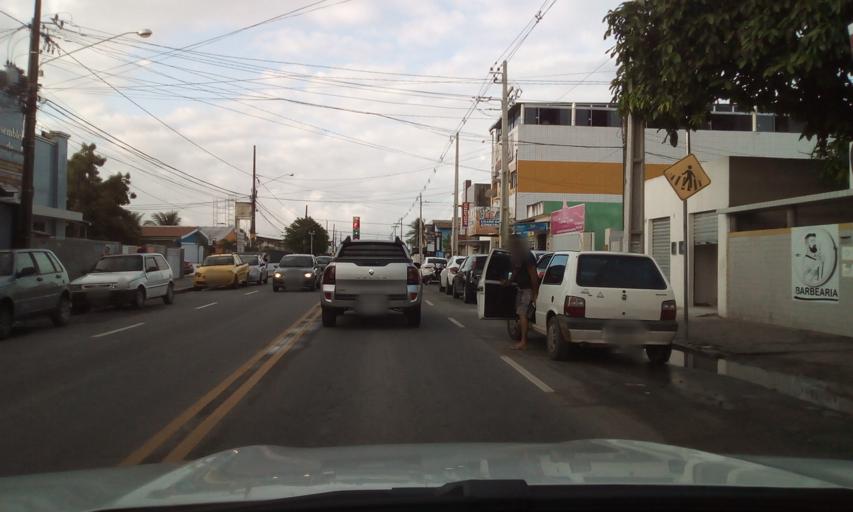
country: BR
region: Paraiba
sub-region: Joao Pessoa
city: Joao Pessoa
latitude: -7.1689
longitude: -34.8422
